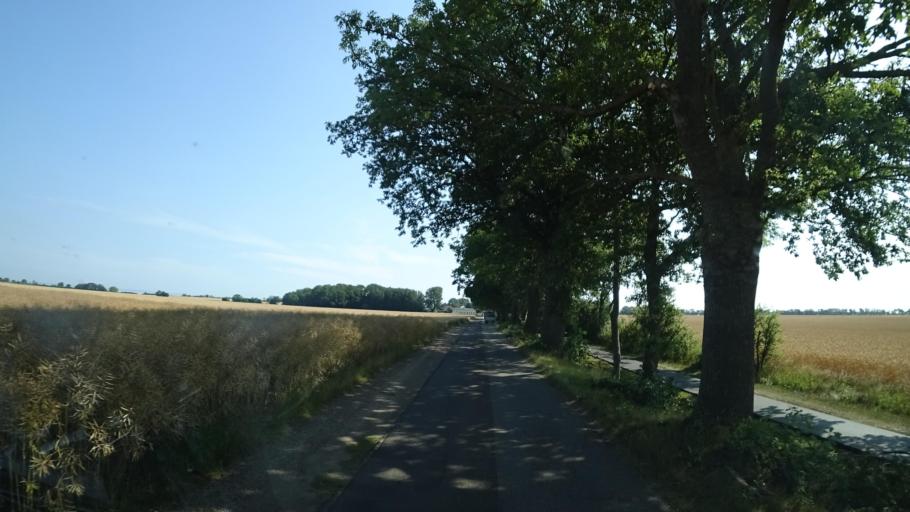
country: DE
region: Mecklenburg-Vorpommern
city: Kemnitz
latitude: 54.1178
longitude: 13.5415
